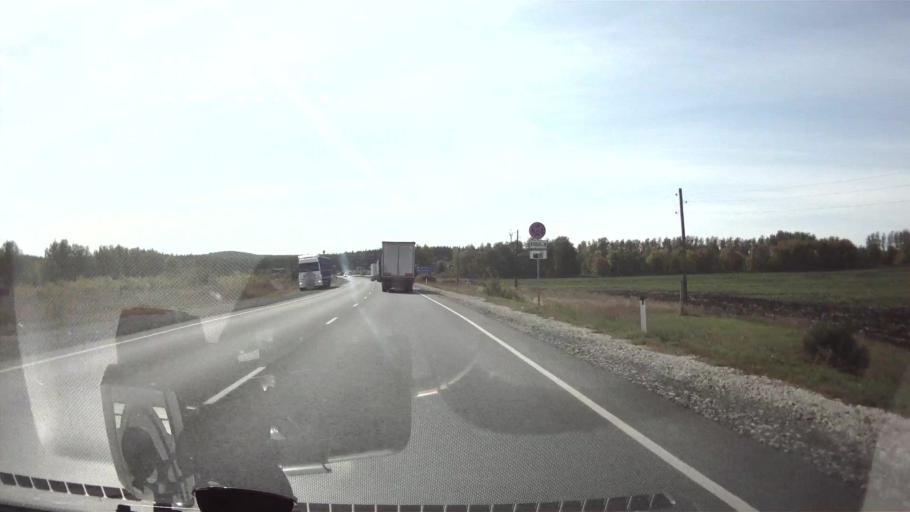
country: RU
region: Saratov
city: Khvalynsk
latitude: 52.5276
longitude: 48.0254
